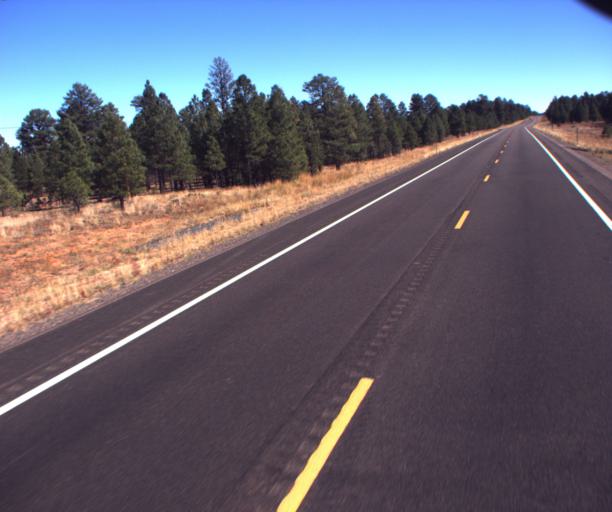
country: US
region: Arizona
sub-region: Apache County
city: Saint Michaels
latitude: 35.6981
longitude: -109.2821
